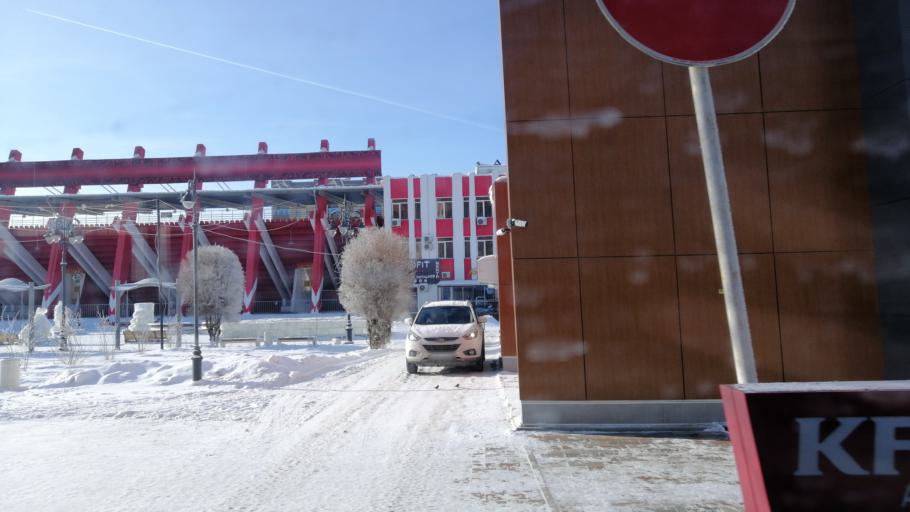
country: KZ
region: Aqtoebe
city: Aqtobe
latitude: 50.2925
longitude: 57.1602
